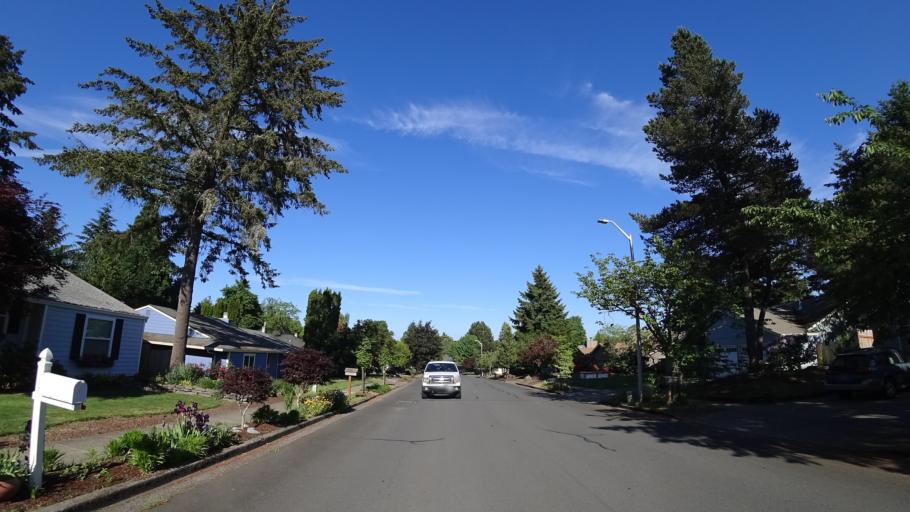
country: US
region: Oregon
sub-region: Washington County
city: Beaverton
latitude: 45.4584
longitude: -122.8124
